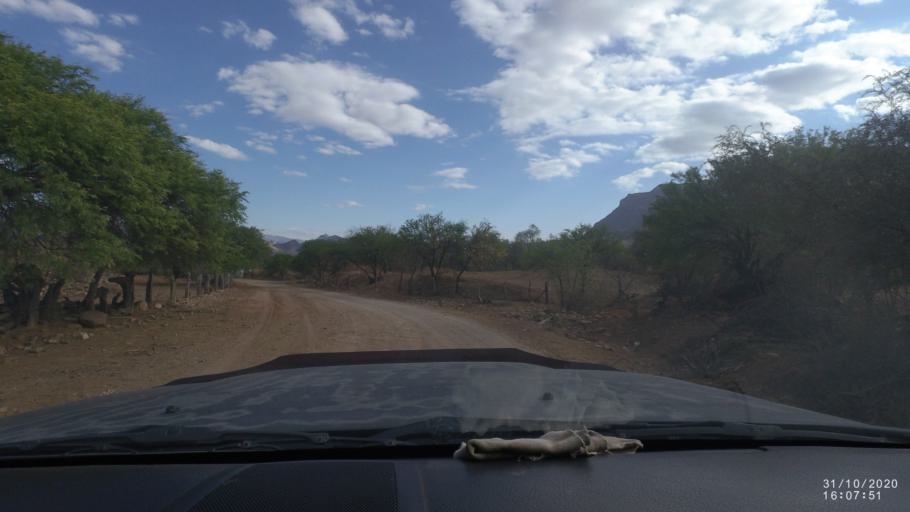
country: BO
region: Chuquisaca
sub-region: Provincia Zudanez
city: Mojocoya
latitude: -18.3828
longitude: -64.6436
